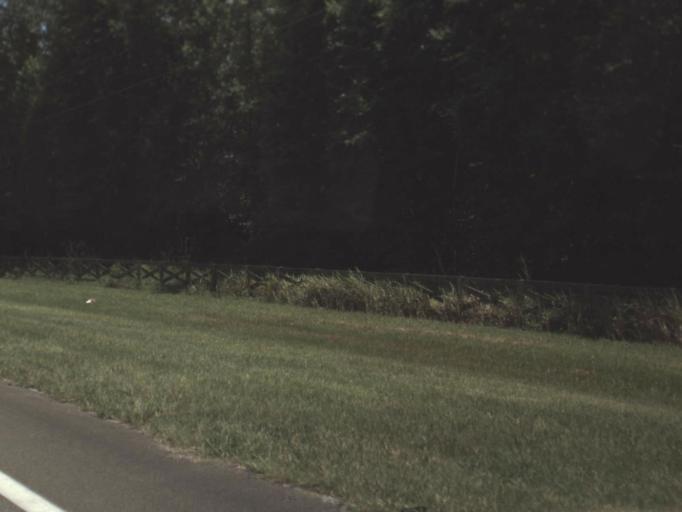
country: US
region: Florida
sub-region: Union County
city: Lake Butler
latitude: 29.9065
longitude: -82.4228
